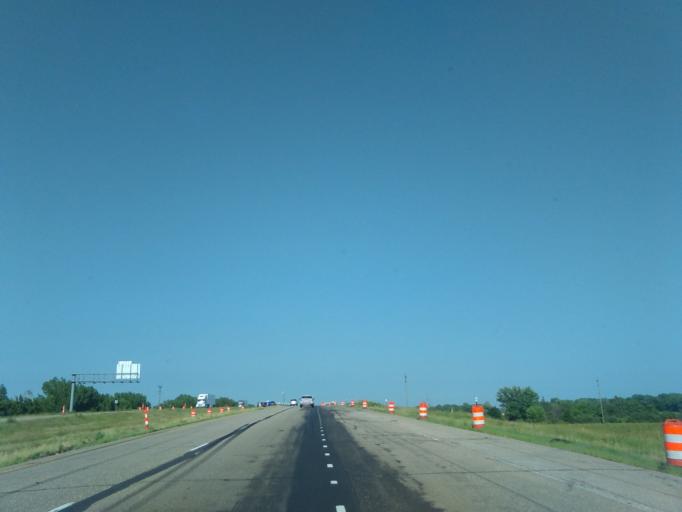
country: US
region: Nebraska
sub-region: Hall County
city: Grand Island
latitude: 40.8215
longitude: -98.3722
